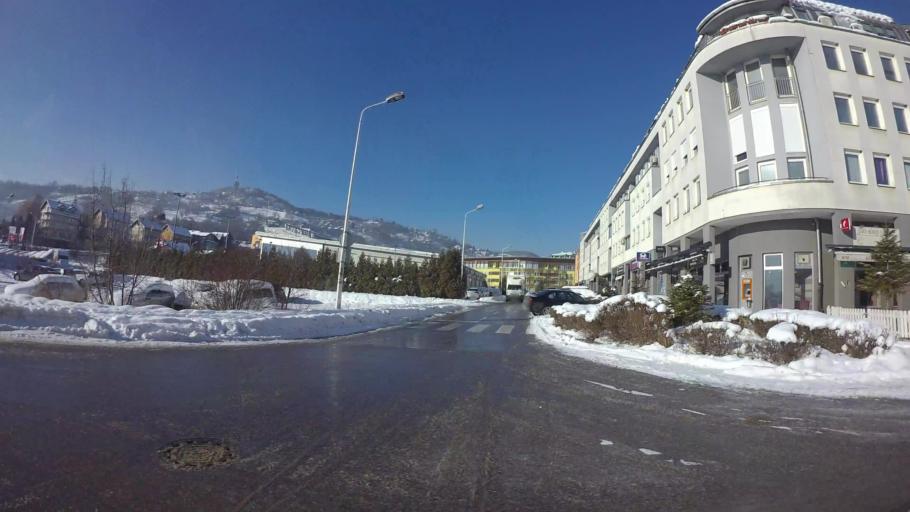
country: BA
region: Federation of Bosnia and Herzegovina
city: Kobilja Glava
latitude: 43.8803
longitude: 18.3995
